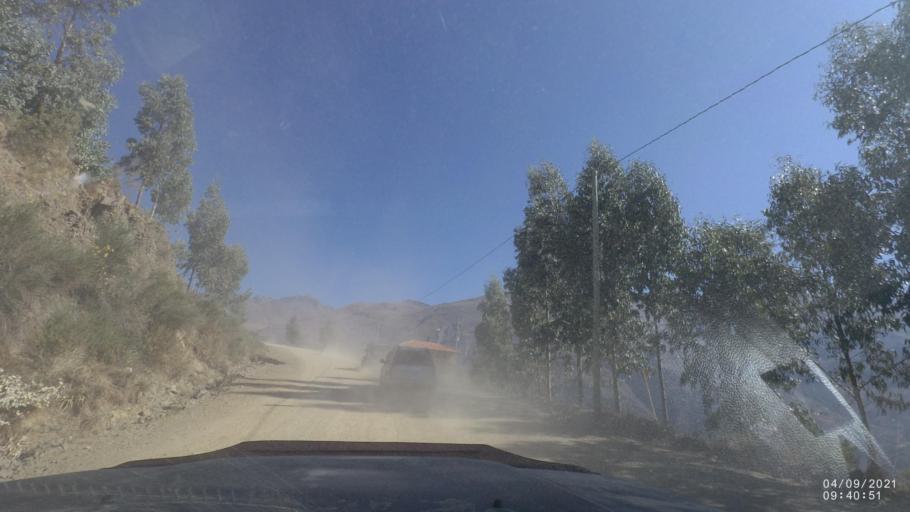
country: BO
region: Cochabamba
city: Sipe Sipe
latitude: -17.3407
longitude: -66.3870
